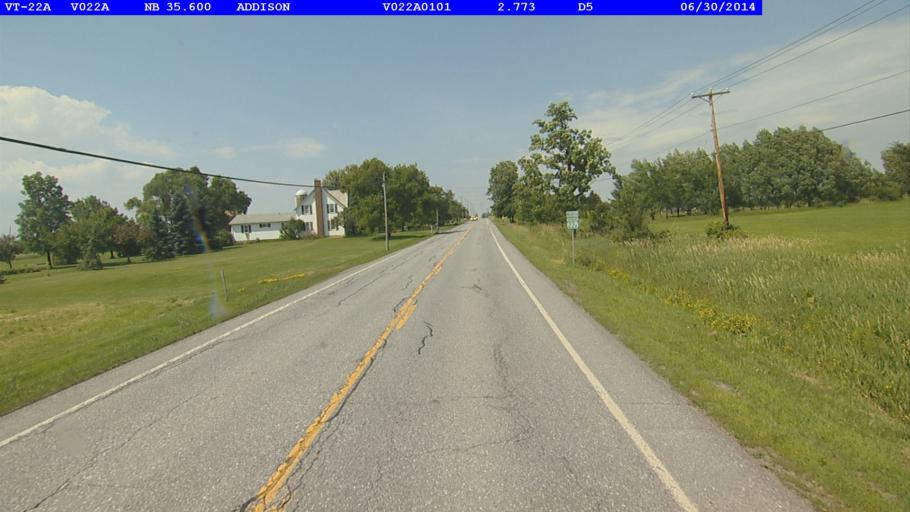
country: US
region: Vermont
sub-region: Addison County
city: Vergennes
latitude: 44.0694
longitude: -73.3043
